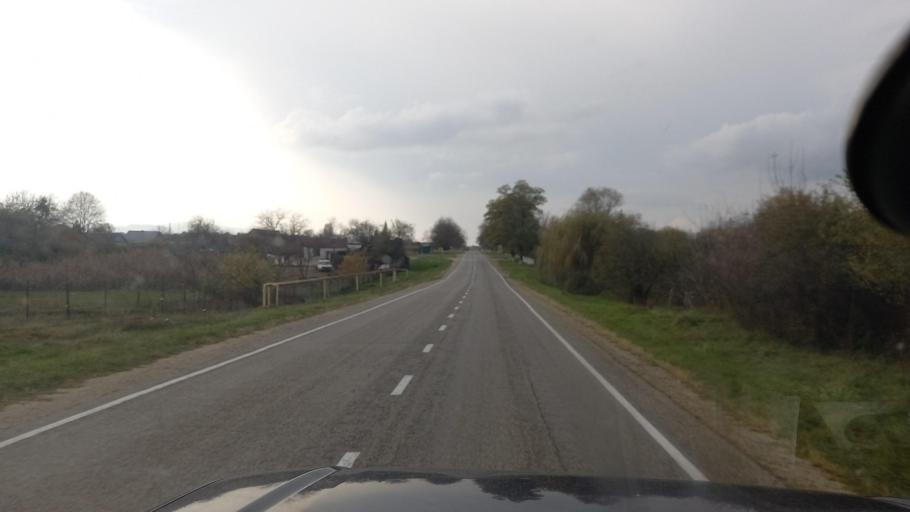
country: RU
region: Krasnodarskiy
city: Gubskaya
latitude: 44.3185
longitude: 40.6175
